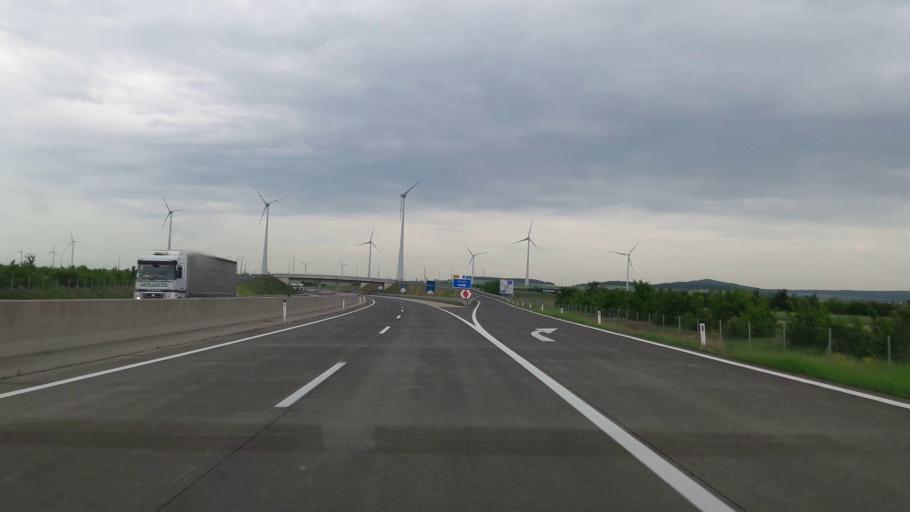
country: AT
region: Lower Austria
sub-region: Politischer Bezirk Bruck an der Leitha
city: Berg
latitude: 48.0796
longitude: 17.0392
